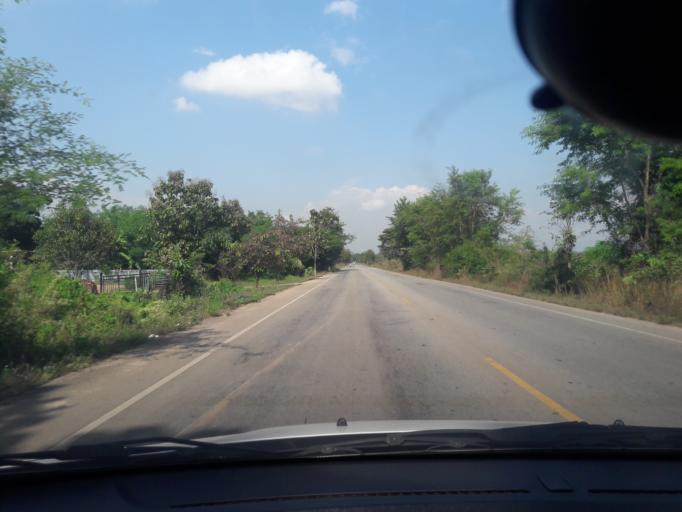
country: TH
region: Lampang
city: Mae Tha
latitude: 18.2027
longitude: 99.5036
